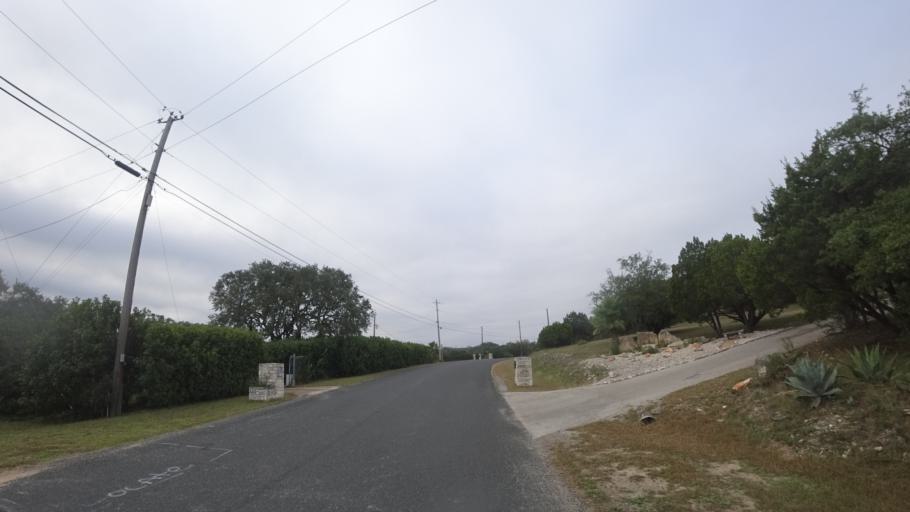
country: US
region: Texas
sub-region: Travis County
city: Hudson Bend
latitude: 30.3908
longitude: -97.9152
